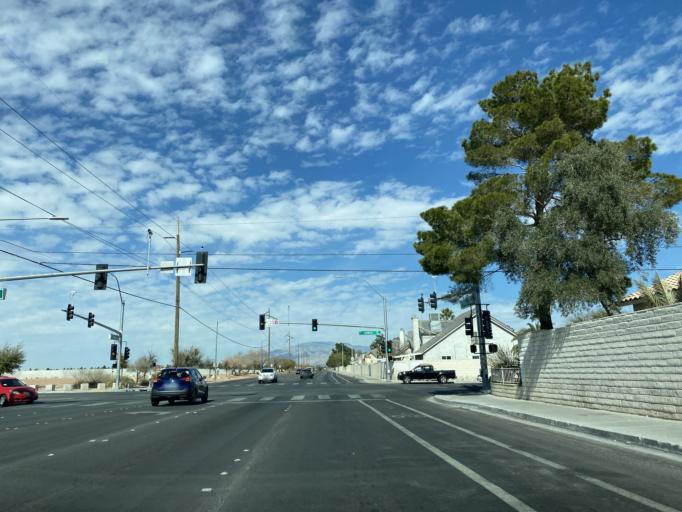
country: US
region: Nevada
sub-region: Clark County
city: Spring Valley
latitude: 36.2252
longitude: -115.2514
